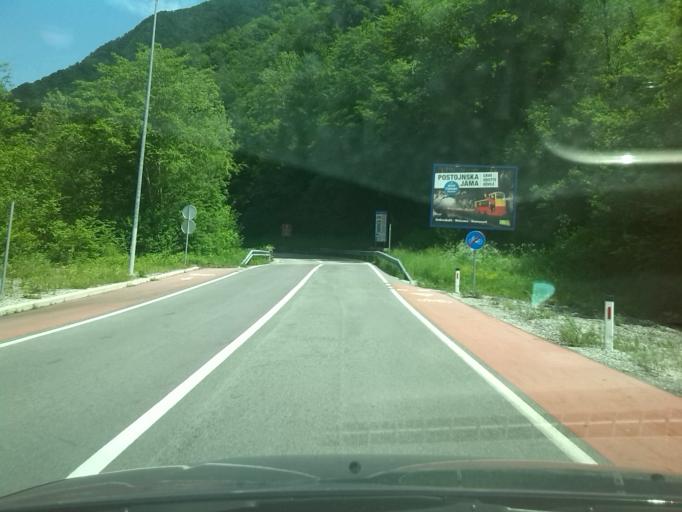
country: IT
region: Friuli Venezia Giulia
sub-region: Provincia di Udine
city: Pulfero
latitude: 46.2189
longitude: 13.5006
